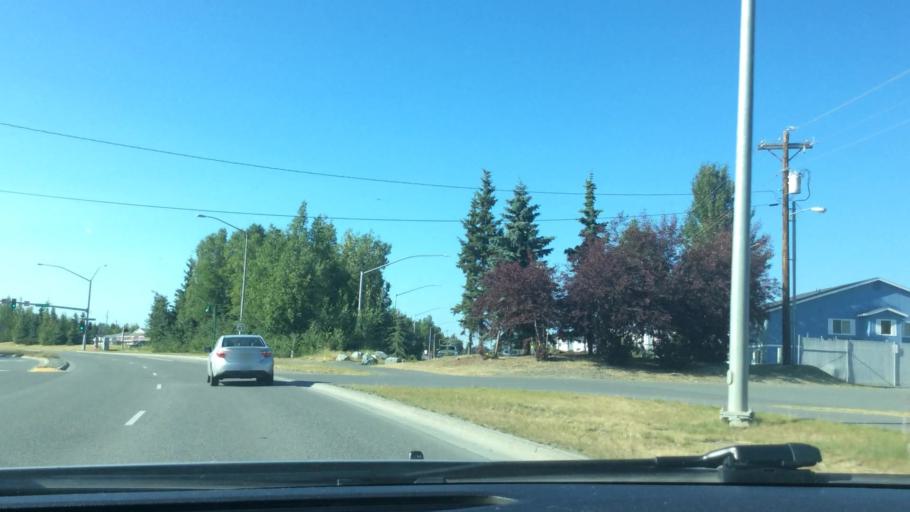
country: US
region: Alaska
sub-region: Anchorage Municipality
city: Anchorage
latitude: 61.1623
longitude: -149.8342
